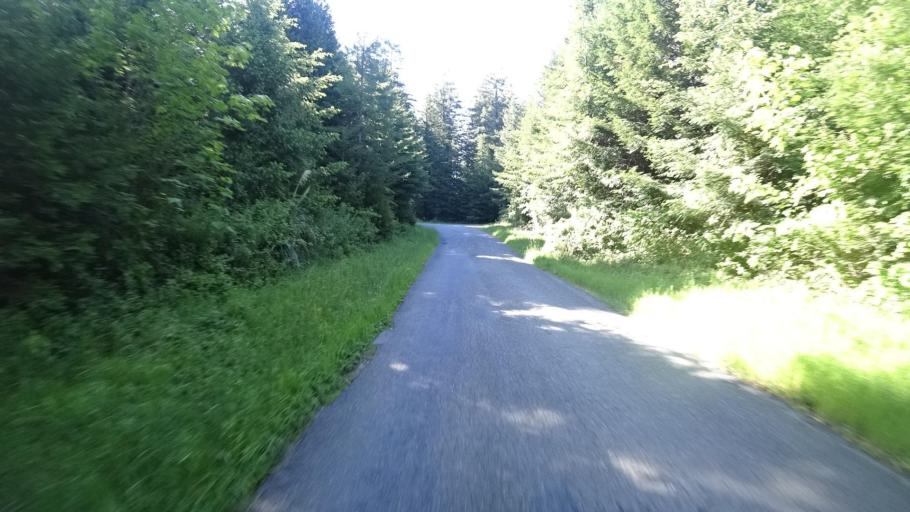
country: US
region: California
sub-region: Humboldt County
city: Rio Dell
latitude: 40.4543
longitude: -124.0308
